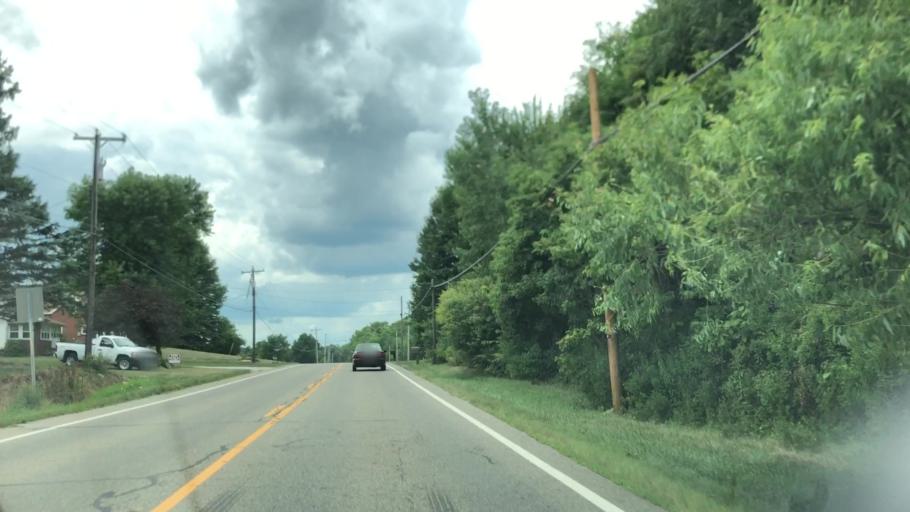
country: US
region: Ohio
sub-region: Summit County
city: Greensburg
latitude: 40.9304
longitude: -81.4516
